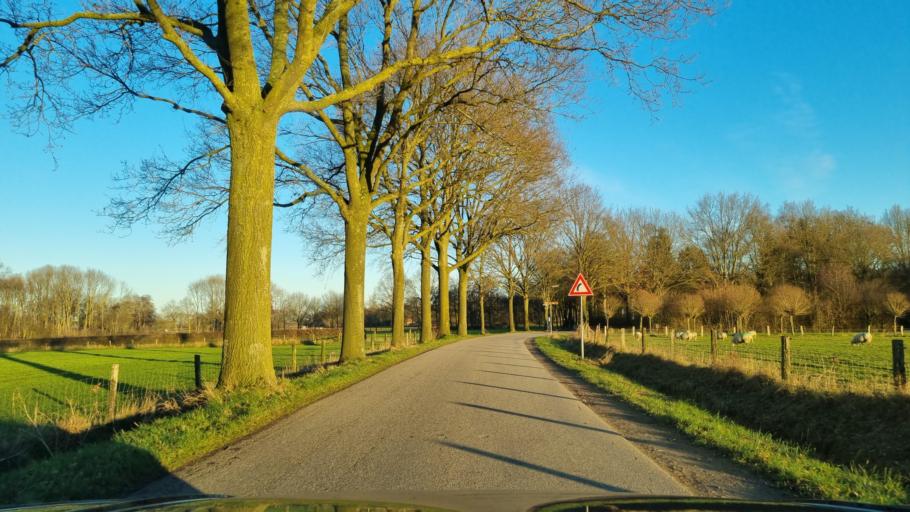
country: NL
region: Gelderland
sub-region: Gemeente Groesbeek
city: De Horst
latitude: 51.7751
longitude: 5.9786
